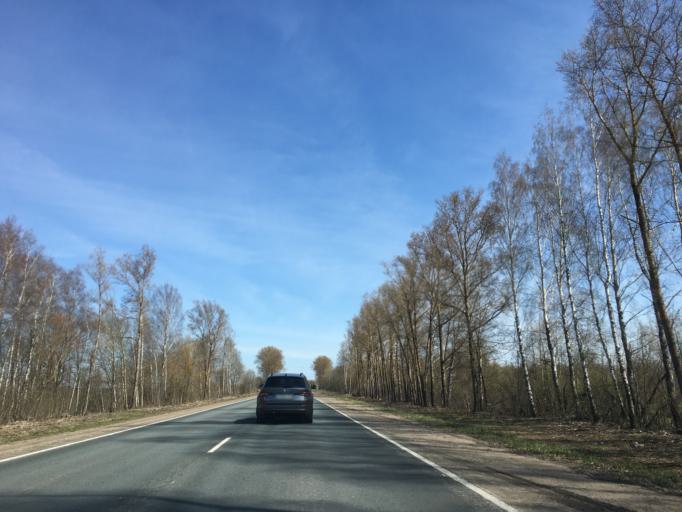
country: RU
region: Pskov
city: Izborsk
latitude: 57.7324
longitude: 27.9801
